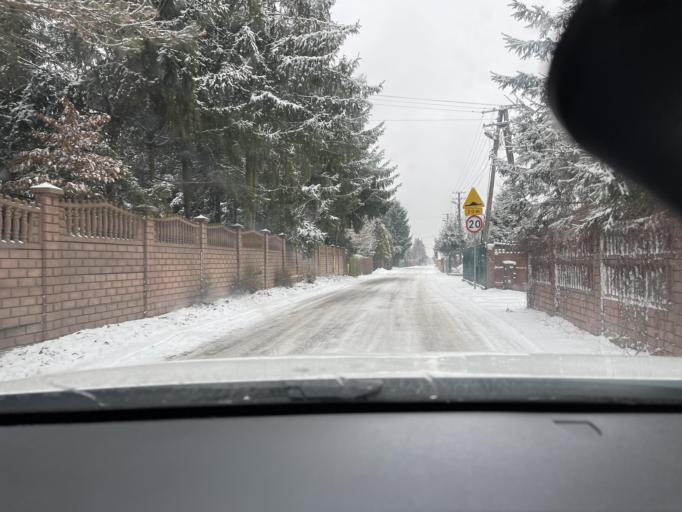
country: PL
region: Masovian Voivodeship
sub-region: Powiat zyrardowski
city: Zyrardow
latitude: 52.0291
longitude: 20.4609
